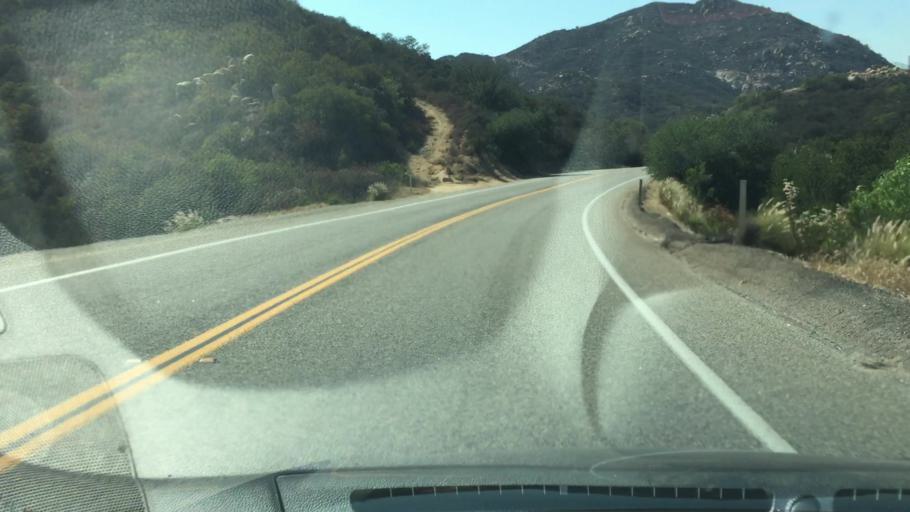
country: US
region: California
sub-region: San Diego County
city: Jamul
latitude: 32.7333
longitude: -116.8241
